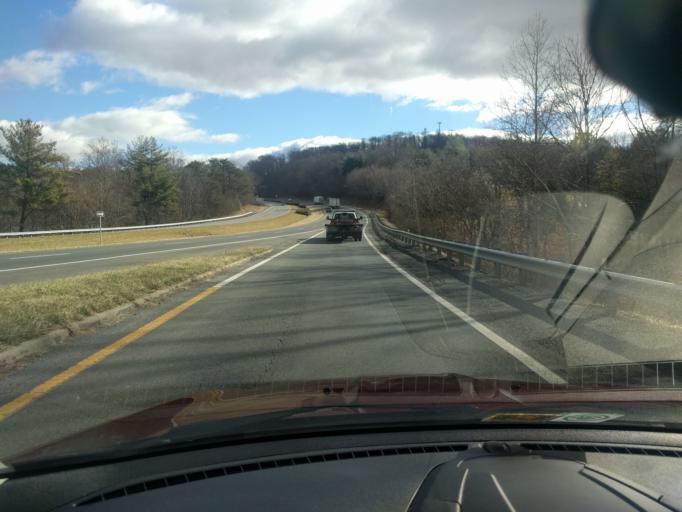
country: US
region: Virginia
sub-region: City of Bedford
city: Bedford
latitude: 37.3230
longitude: -79.5303
